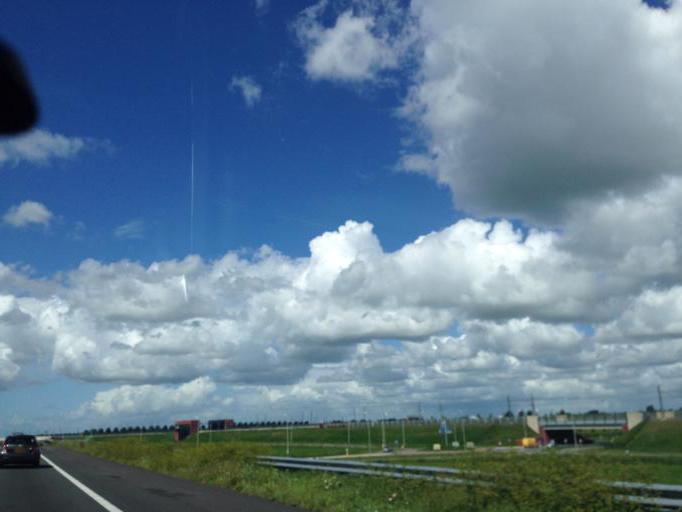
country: NL
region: Overijssel
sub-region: Gemeente Kampen
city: Kampen
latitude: 52.5291
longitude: 5.9164
